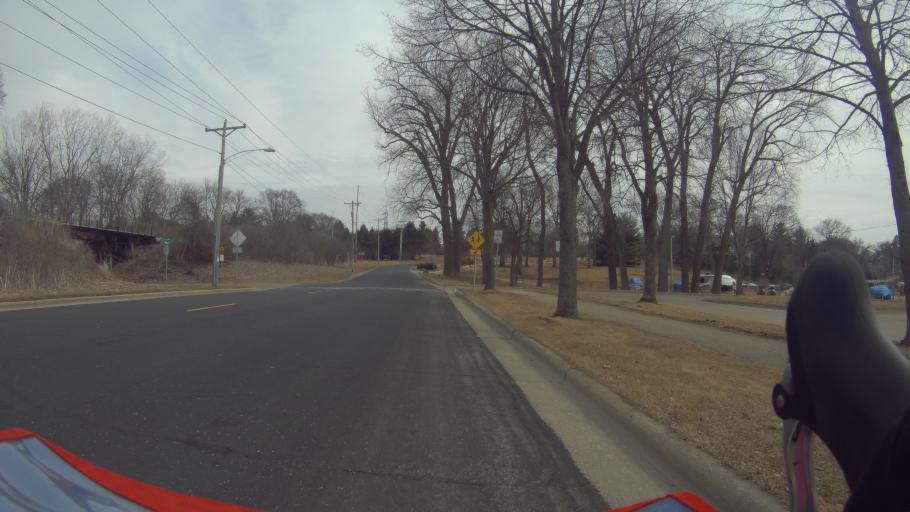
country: US
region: Wisconsin
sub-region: Dane County
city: Maple Bluff
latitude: 43.1248
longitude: -89.3753
